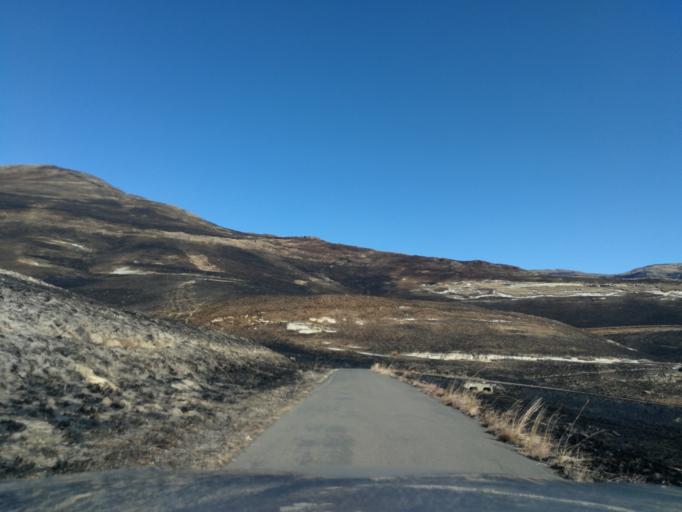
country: ZA
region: Orange Free State
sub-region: Thabo Mofutsanyana District Municipality
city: Phuthaditjhaba
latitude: -28.5206
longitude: 28.6217
